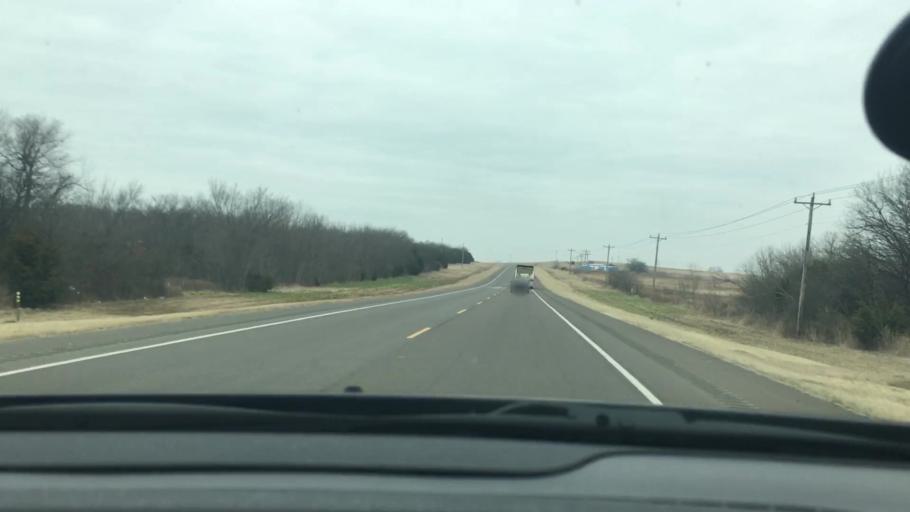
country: US
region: Oklahoma
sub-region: Murray County
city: Davis
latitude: 34.5162
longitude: -97.2052
